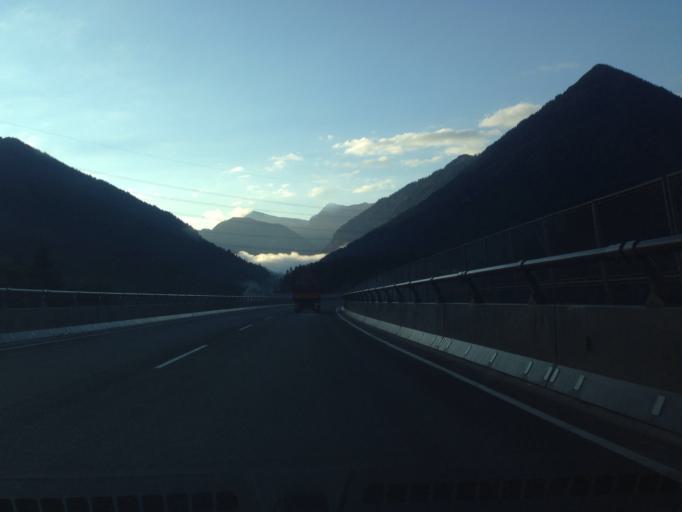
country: AT
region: Tyrol
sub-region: Politischer Bezirk Reutte
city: Breitenwang
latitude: 47.4965
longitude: 10.7436
